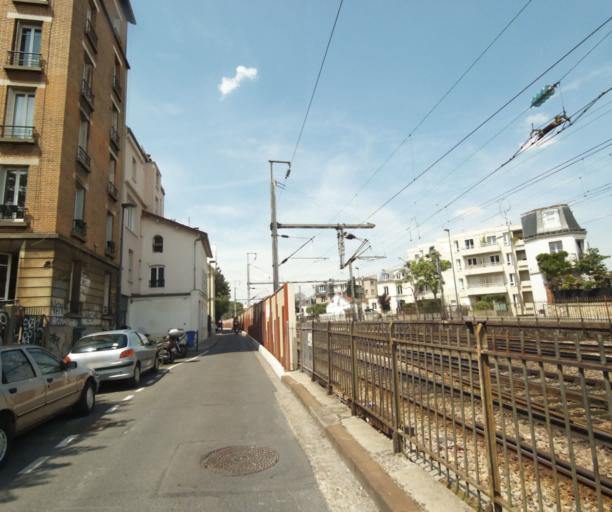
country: FR
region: Ile-de-France
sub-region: Departement des Hauts-de-Seine
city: Asnieres-sur-Seine
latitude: 48.9065
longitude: 2.2797
